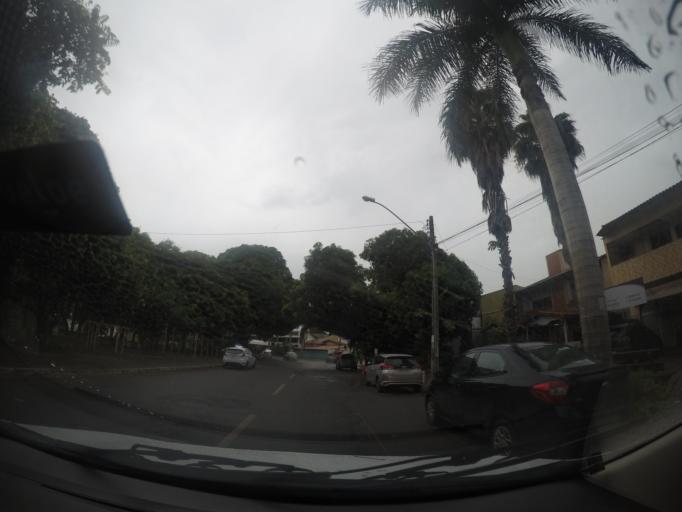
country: BR
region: Goias
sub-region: Goiania
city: Goiania
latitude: -16.6496
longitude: -49.2284
